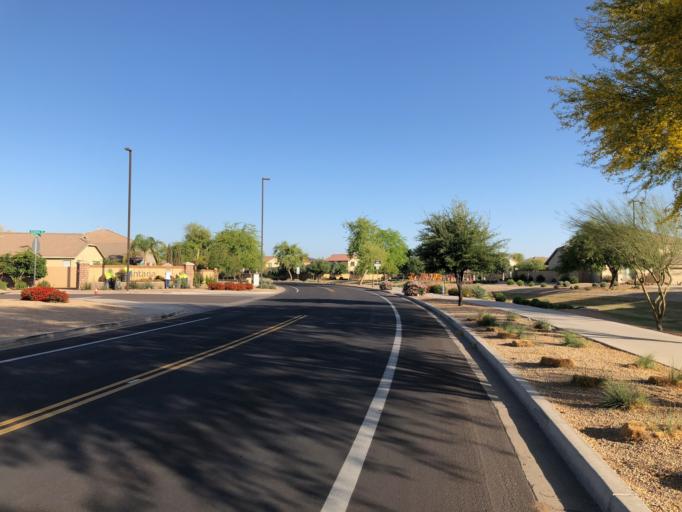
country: US
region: Arizona
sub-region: Maricopa County
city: Queen Creek
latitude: 33.2262
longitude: -111.7121
